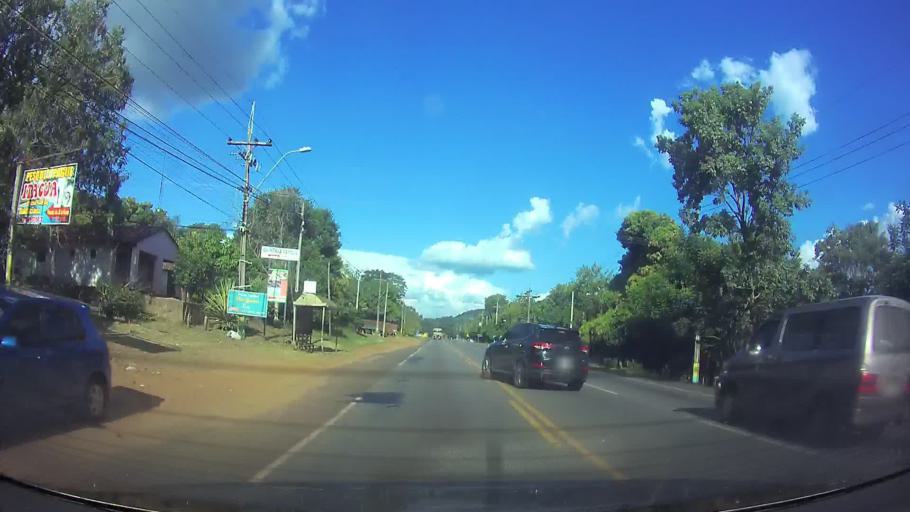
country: PY
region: Cordillera
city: Caacupe
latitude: -25.3881
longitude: -57.1104
